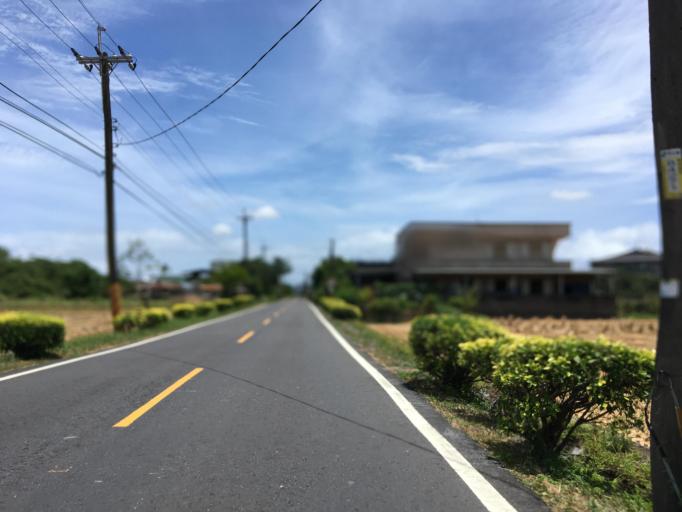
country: TW
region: Taiwan
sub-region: Yilan
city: Yilan
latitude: 24.6545
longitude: 121.7291
